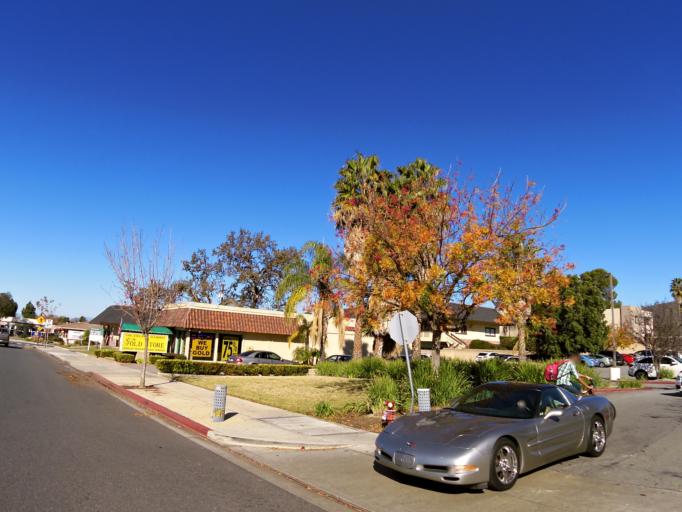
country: US
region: California
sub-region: Ventura County
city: Thousand Oaks
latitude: 34.1729
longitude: -118.8409
